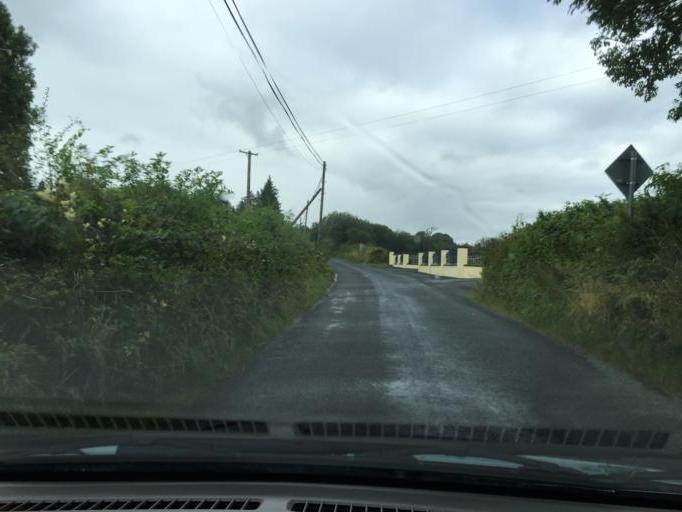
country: IE
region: Connaught
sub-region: Sligo
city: Tobercurry
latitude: 54.0381
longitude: -8.8449
